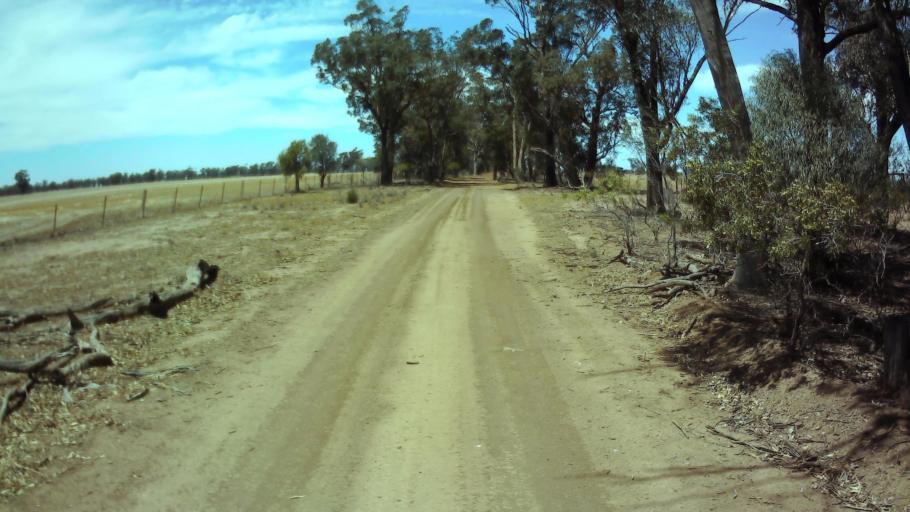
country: AU
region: New South Wales
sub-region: Weddin
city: Grenfell
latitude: -33.9220
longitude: 147.8045
